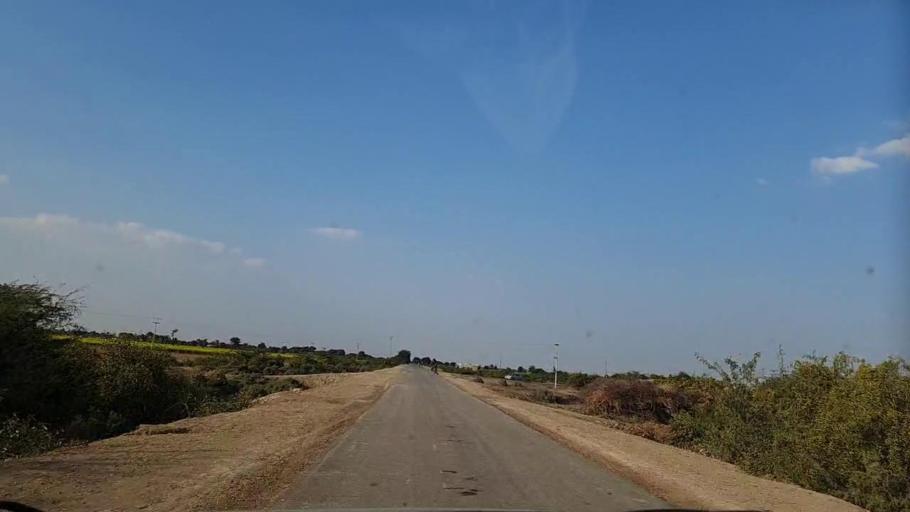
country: PK
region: Sindh
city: Pithoro
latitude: 25.6793
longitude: 69.2268
